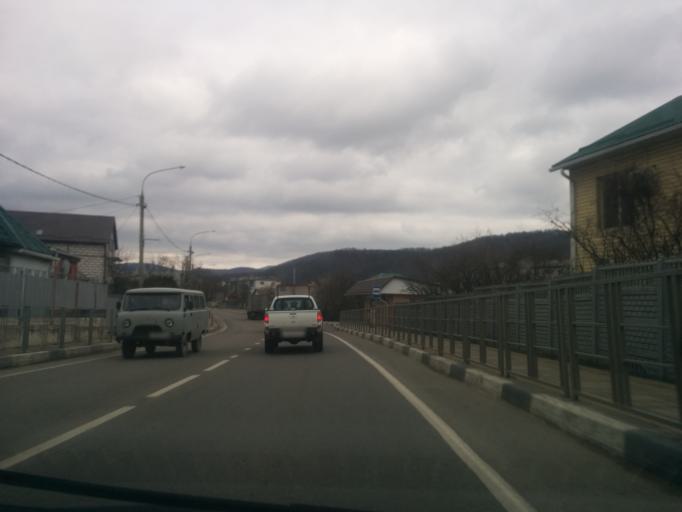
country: RU
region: Krasnodarskiy
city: Novomikhaylovskiy
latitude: 44.2517
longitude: 38.8393
